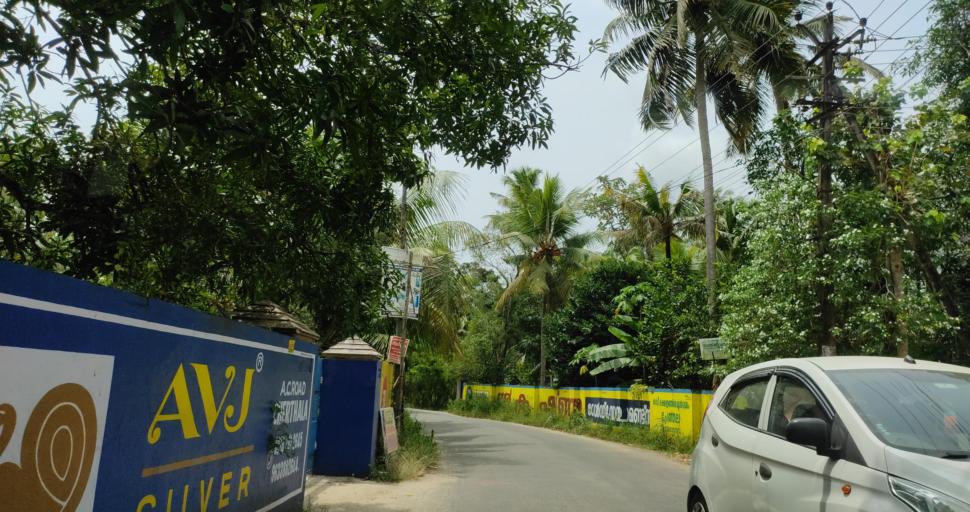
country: IN
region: Kerala
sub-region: Alappuzha
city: Shertallai
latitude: 9.6750
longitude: 76.3549
